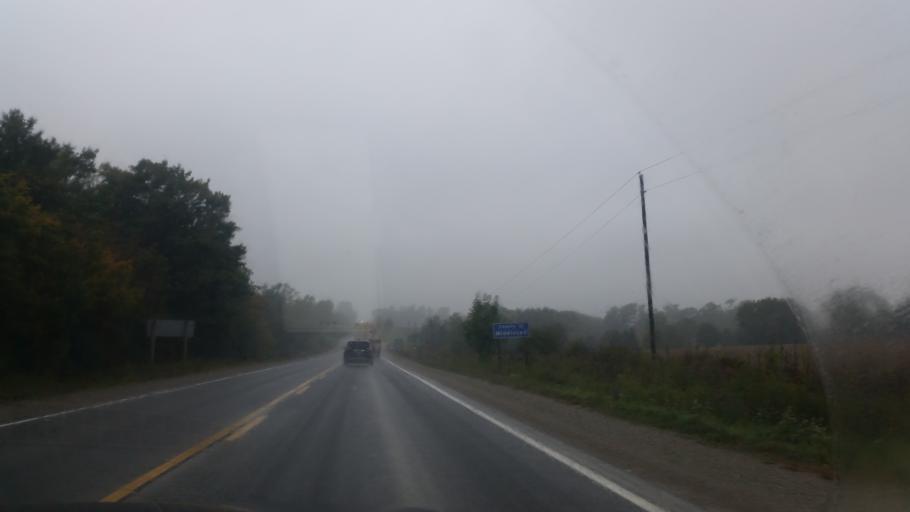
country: CA
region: Ontario
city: London
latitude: 43.2038
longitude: -81.2229
